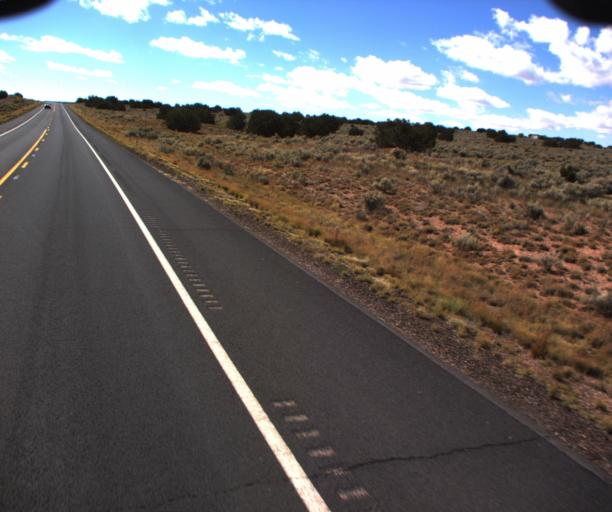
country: US
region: Arizona
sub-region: Apache County
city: Houck
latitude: 35.1803
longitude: -109.3377
